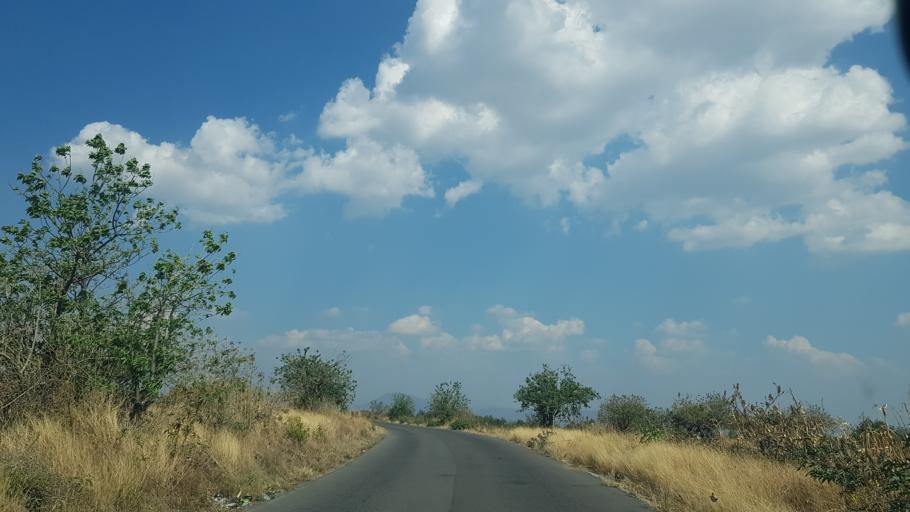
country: MX
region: Puebla
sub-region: Atlixco
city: Colonia Agricola de Ocotepec (Colonia San Jose)
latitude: 18.9185
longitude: -98.5295
